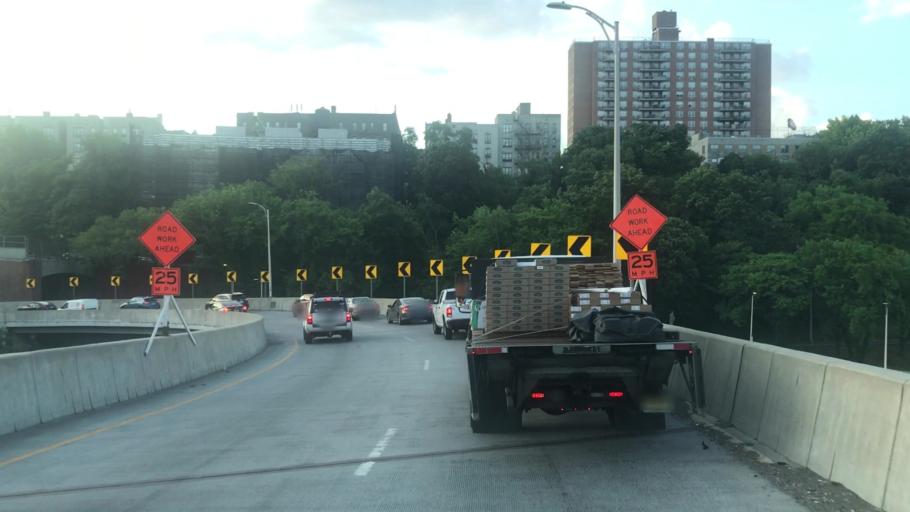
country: US
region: New York
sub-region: New York County
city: Inwood
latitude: 40.8447
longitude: -73.9268
